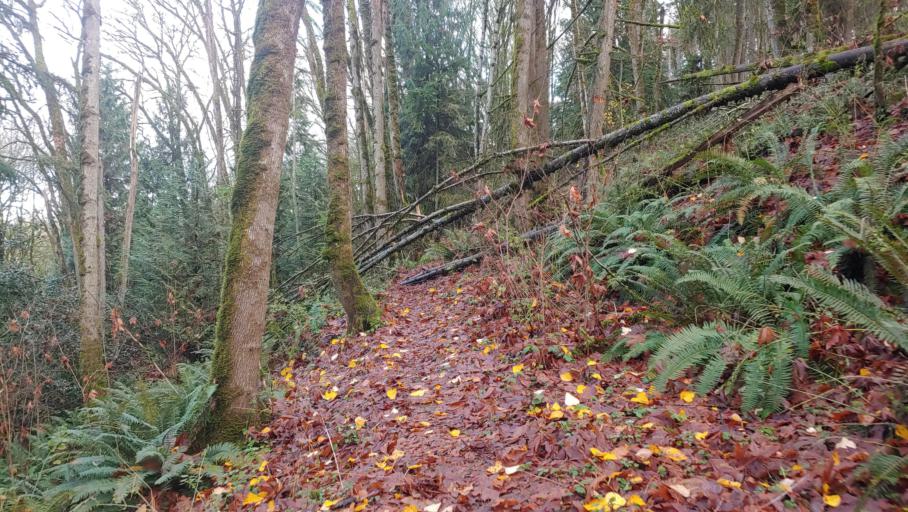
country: US
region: Washington
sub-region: King County
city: Eastgate
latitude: 47.5695
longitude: -122.1517
